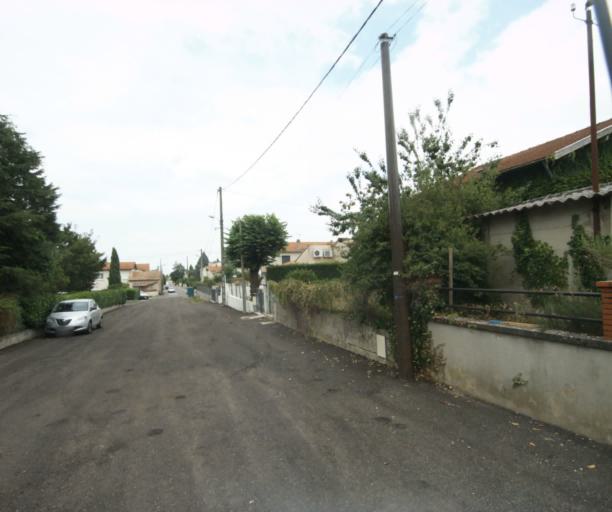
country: FR
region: Midi-Pyrenees
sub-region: Departement de la Haute-Garonne
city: Revel
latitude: 43.4527
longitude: 2.0102
